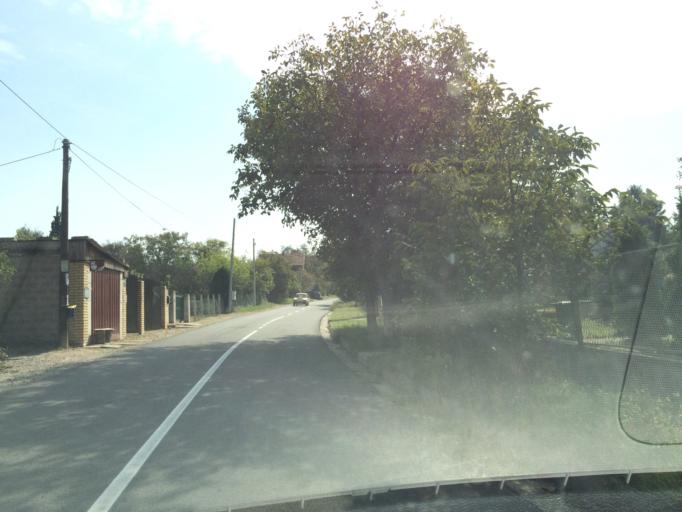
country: RS
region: Autonomna Pokrajina Vojvodina
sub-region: Juznobacki Okrug
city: Novi Sad
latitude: 45.1917
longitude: 19.8344
